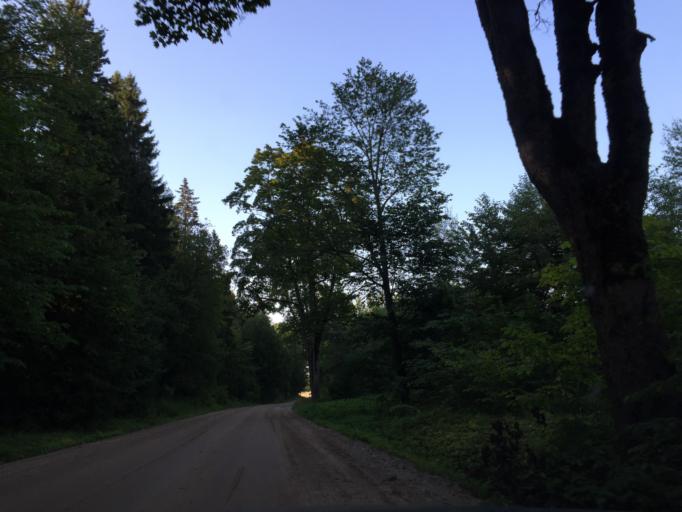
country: LV
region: Limbazu Rajons
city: Limbazi
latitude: 57.5589
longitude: 24.8057
